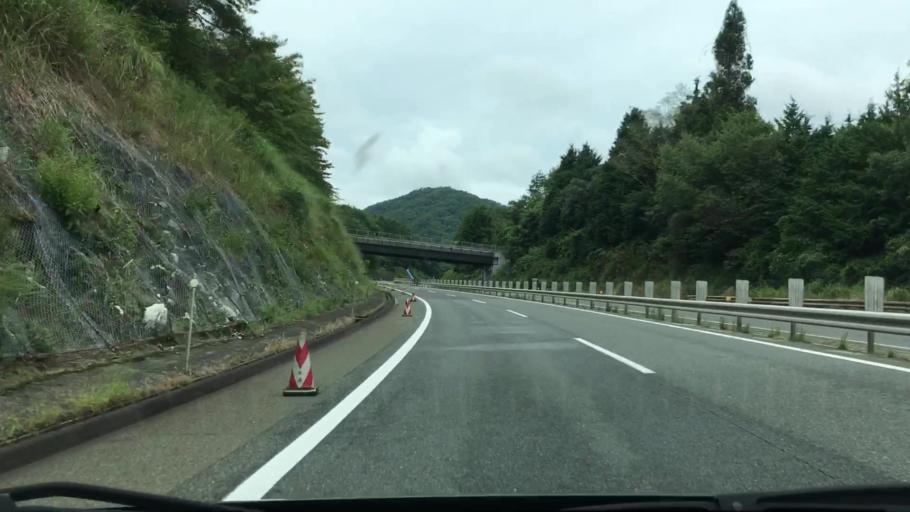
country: JP
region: Hiroshima
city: Shobara
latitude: 34.8734
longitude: 133.1730
